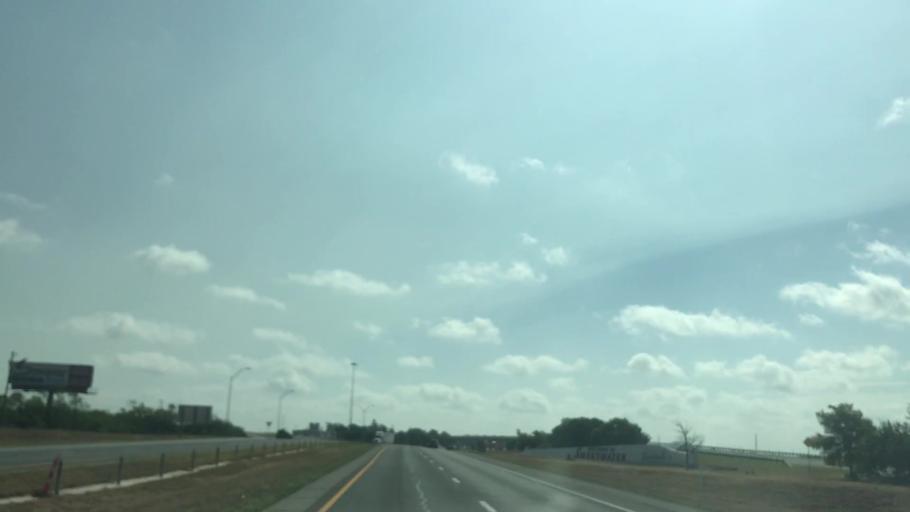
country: US
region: Texas
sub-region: Nolan County
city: Sweetwater
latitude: 32.4532
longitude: -100.4684
